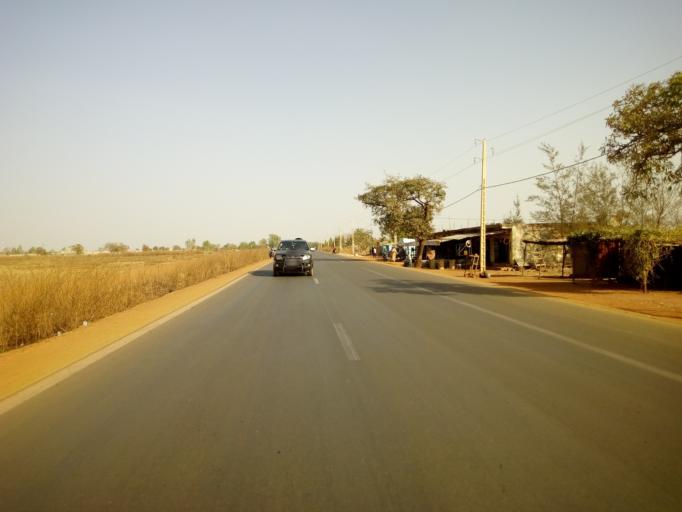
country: ML
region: Bamako
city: Bamako
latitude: 12.5835
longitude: -7.8215
